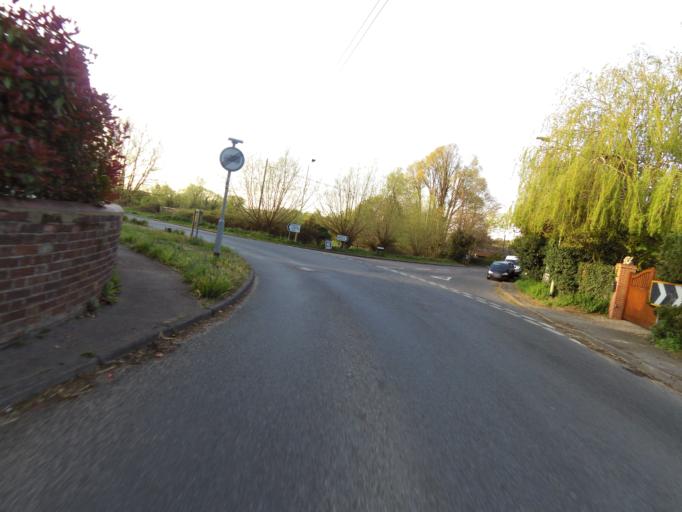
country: GB
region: England
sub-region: Suffolk
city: Bramford
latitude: 52.0392
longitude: 1.0895
